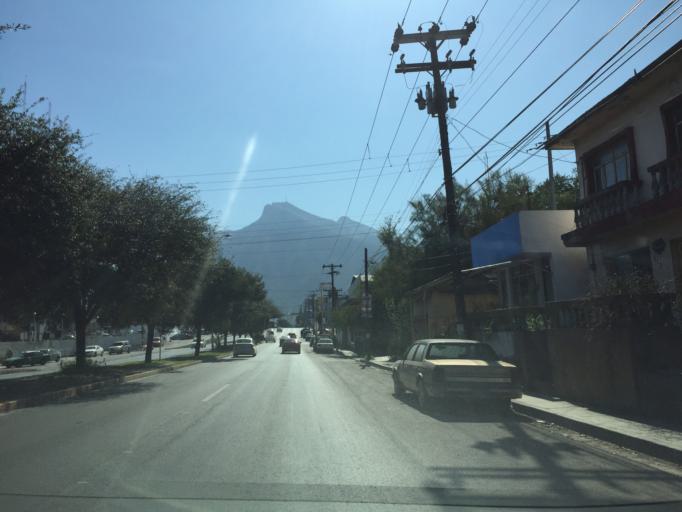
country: MX
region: Nuevo Leon
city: Guadalupe
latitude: 25.6852
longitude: -100.2304
